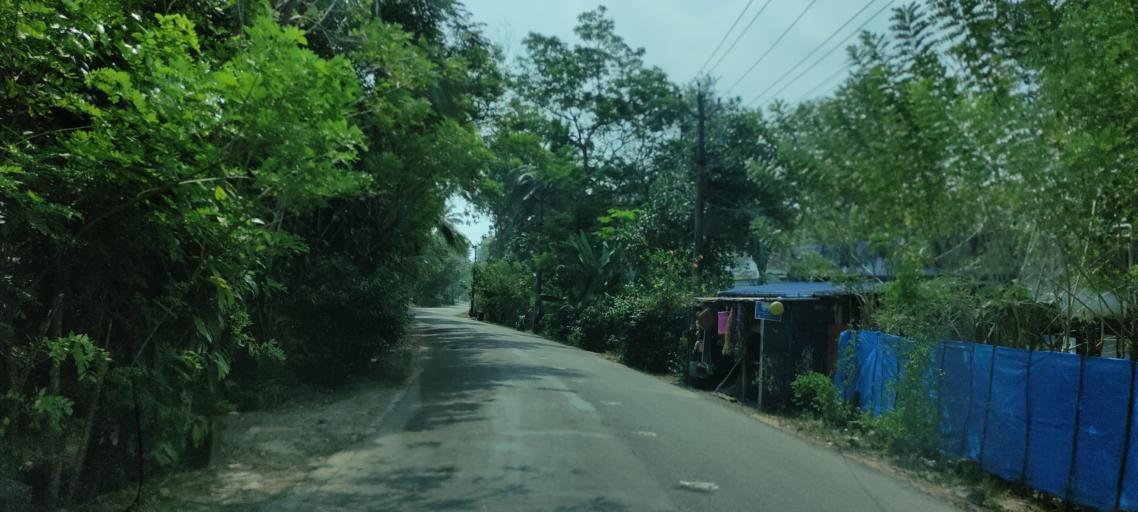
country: IN
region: Kerala
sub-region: Alappuzha
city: Shertallai
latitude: 9.6335
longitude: 76.3523
